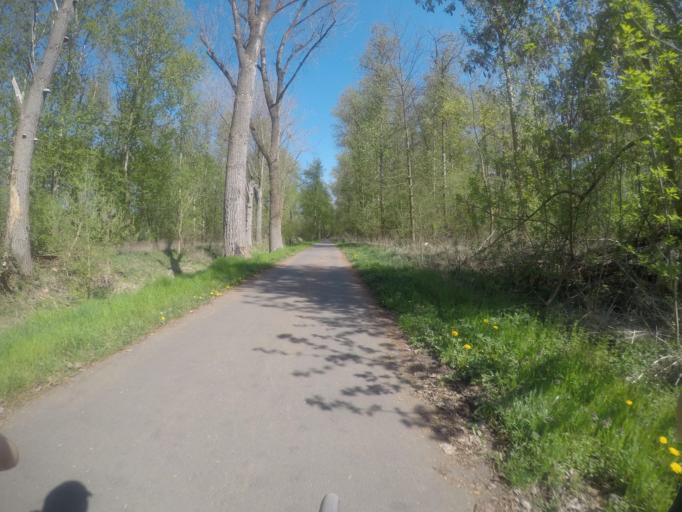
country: DE
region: Brandenburg
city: Bernau bei Berlin
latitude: 52.6689
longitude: 13.5725
